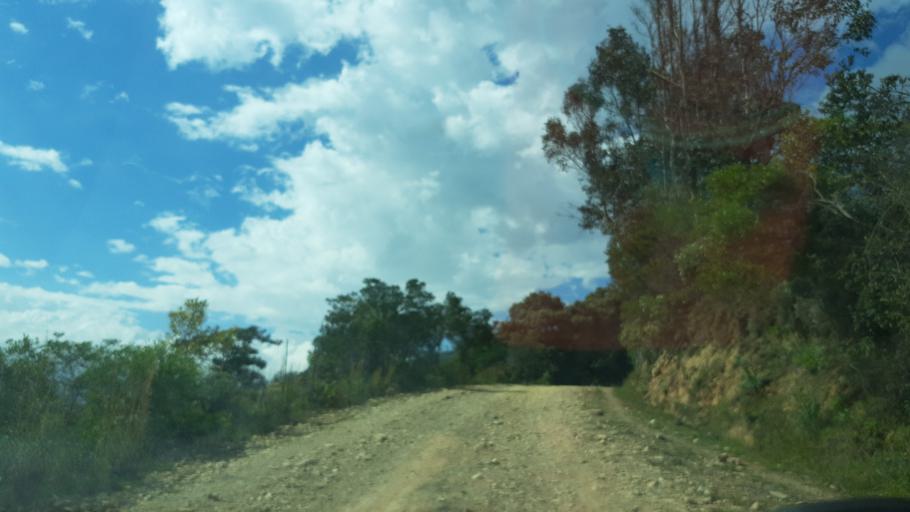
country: CO
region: Boyaca
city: Santa Sofia
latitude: 5.7209
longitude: -73.5408
